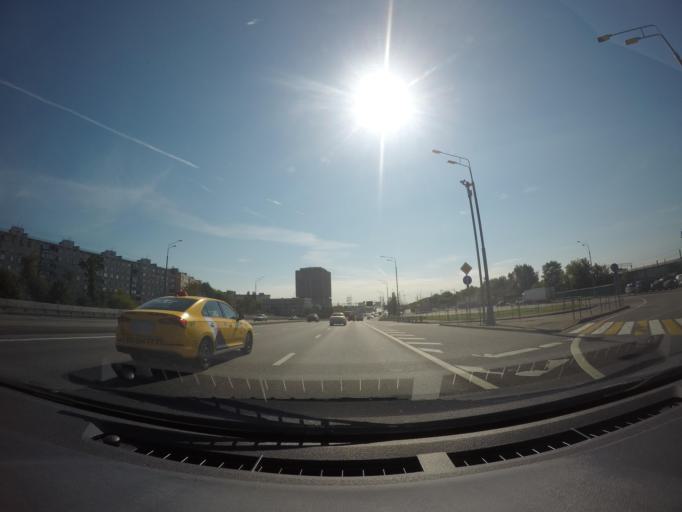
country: RU
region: Moscow
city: Veshnyaki
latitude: 55.7147
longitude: 37.8246
